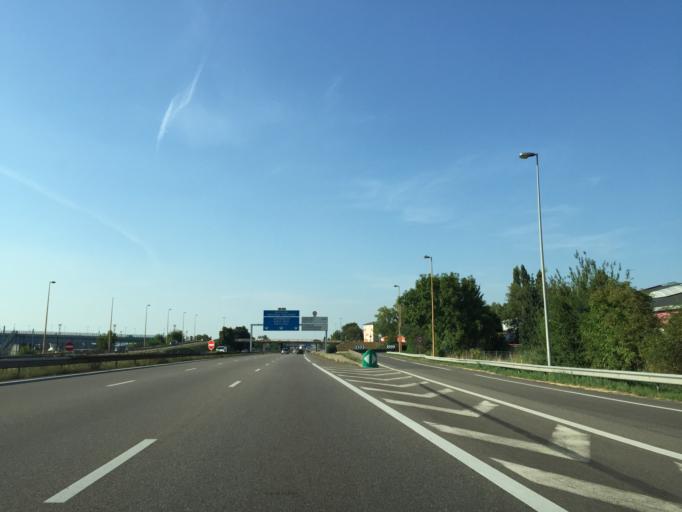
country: FR
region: Alsace
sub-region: Departement du Bas-Rhin
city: Schiltigheim
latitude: 48.6126
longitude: 7.7268
